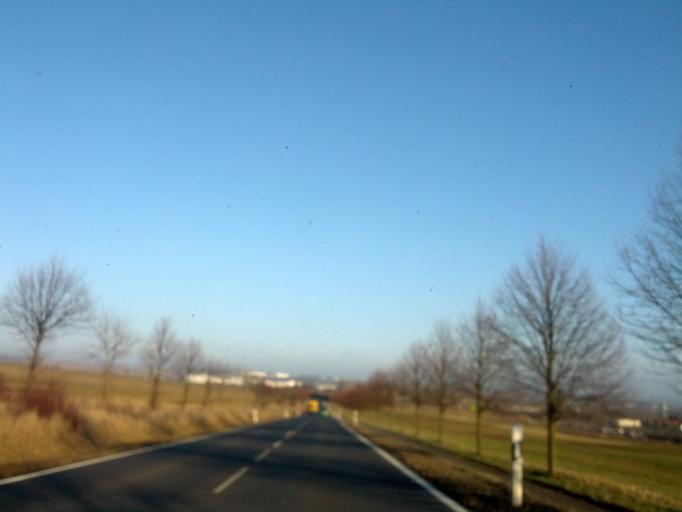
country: DE
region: Thuringia
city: Bischofroda
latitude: 50.9958
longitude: 10.3758
